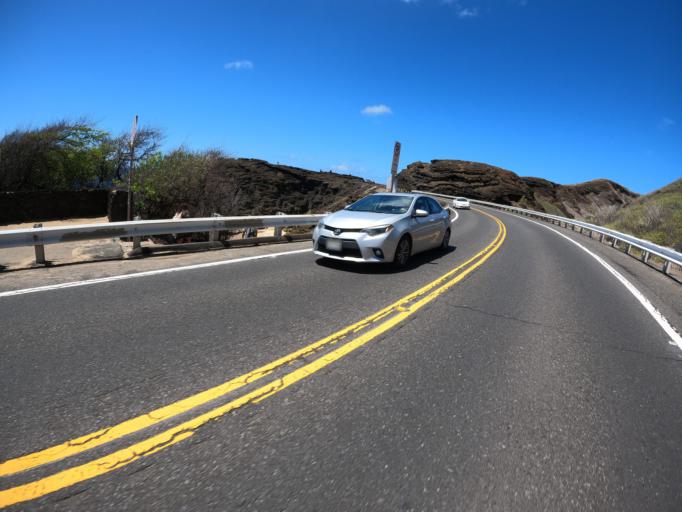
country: US
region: Hawaii
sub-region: Honolulu County
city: Waimanalo Beach
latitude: 21.2823
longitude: -157.6778
